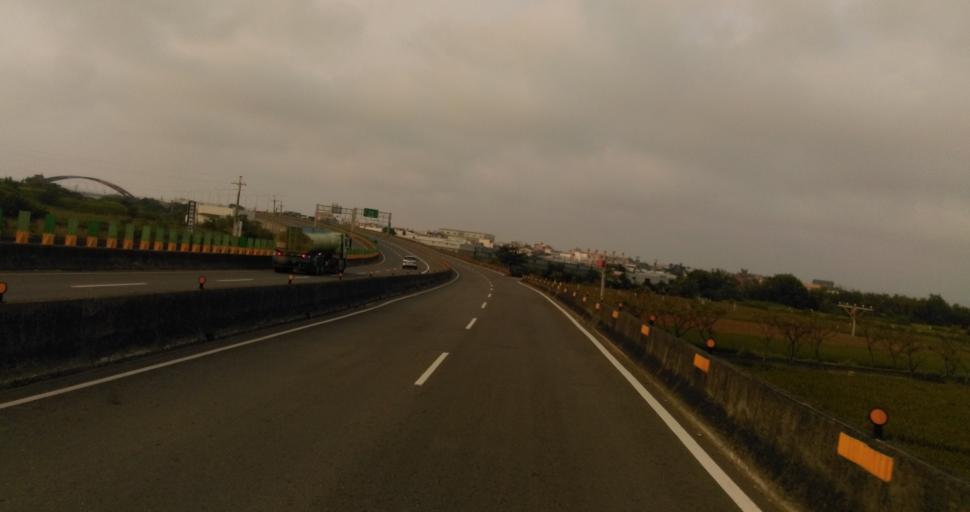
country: TW
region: Taiwan
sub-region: Hsinchu
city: Hsinchu
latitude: 24.8003
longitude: 120.9207
